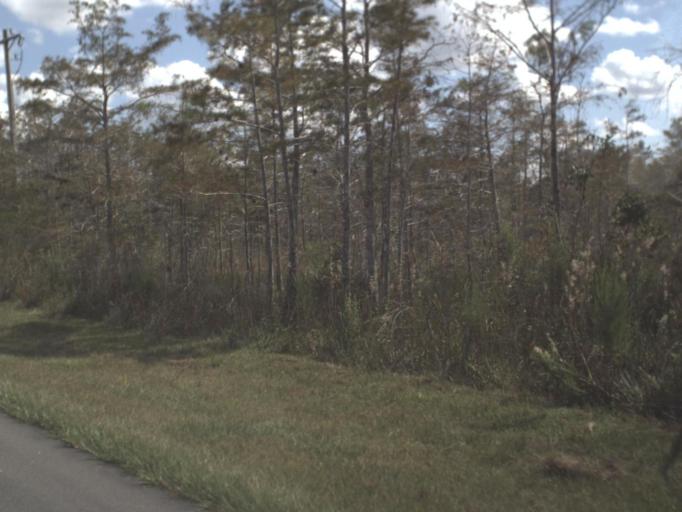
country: US
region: Florida
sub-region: Miami-Dade County
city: Kendall West
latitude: 25.8452
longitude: -80.9205
